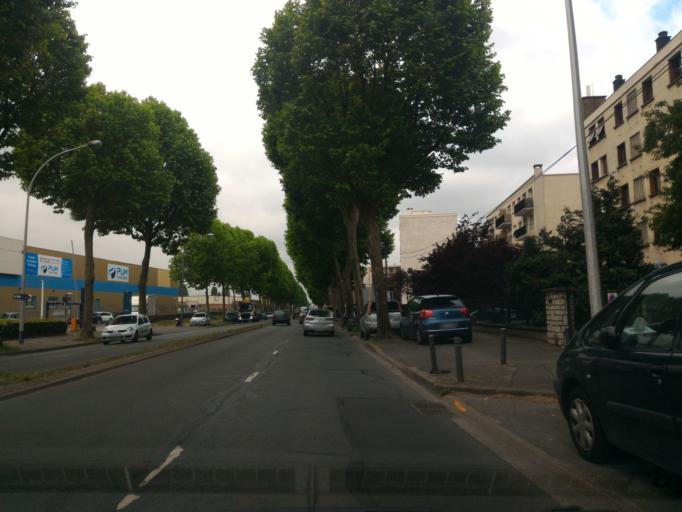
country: FR
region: Ile-de-France
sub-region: Departement du Val-de-Marne
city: Chevilly-Larue
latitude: 48.7655
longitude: 2.3351
